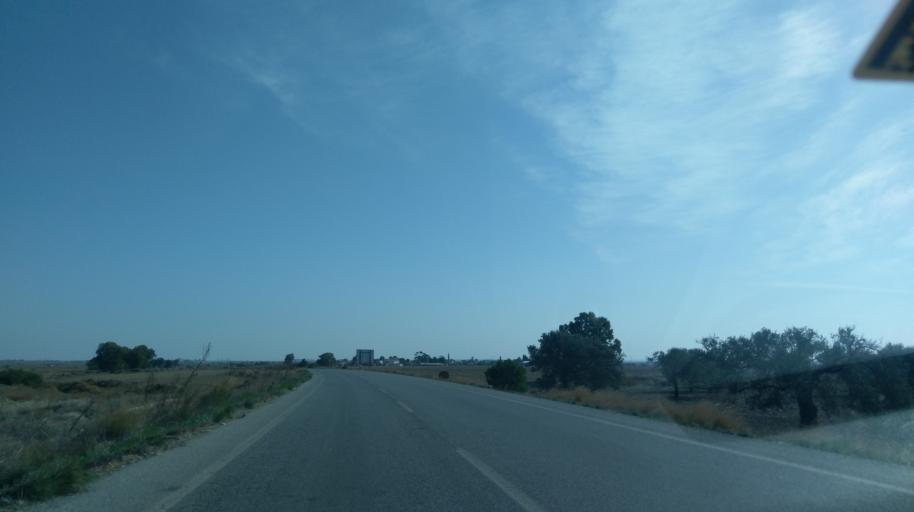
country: CY
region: Ammochostos
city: Lefkonoiko
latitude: 35.2589
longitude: 33.6730
